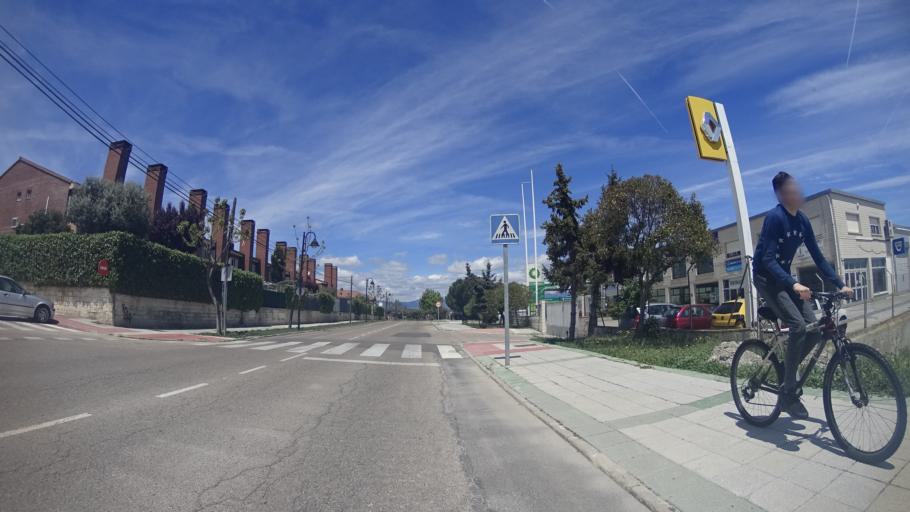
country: ES
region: Madrid
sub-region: Provincia de Madrid
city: Galapagar
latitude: 40.5833
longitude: -4.0100
